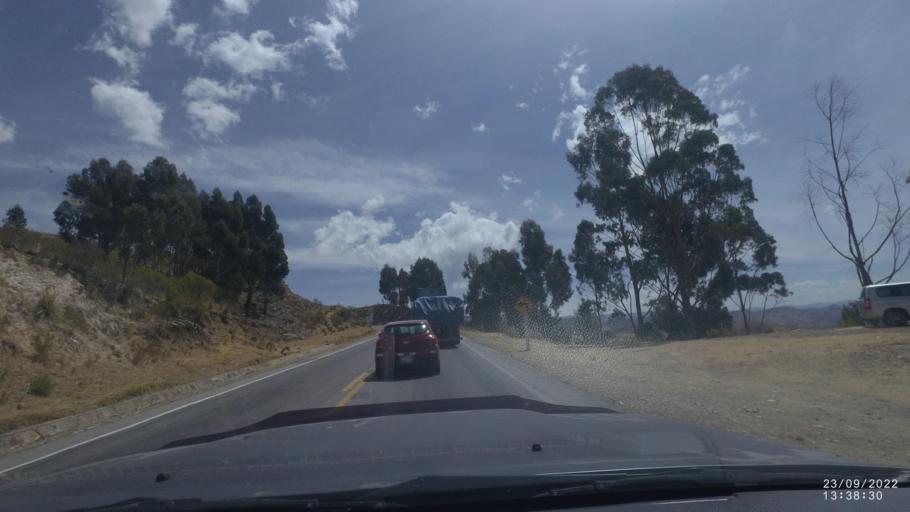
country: BO
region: Cochabamba
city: Sipe Sipe
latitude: -17.6506
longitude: -66.4814
